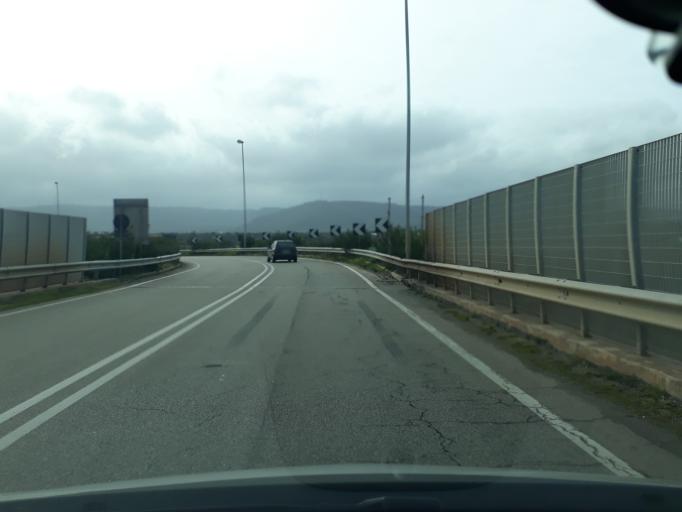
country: IT
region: Apulia
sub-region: Provincia di Bari
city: Monopoli
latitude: 40.9220
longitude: 17.3158
